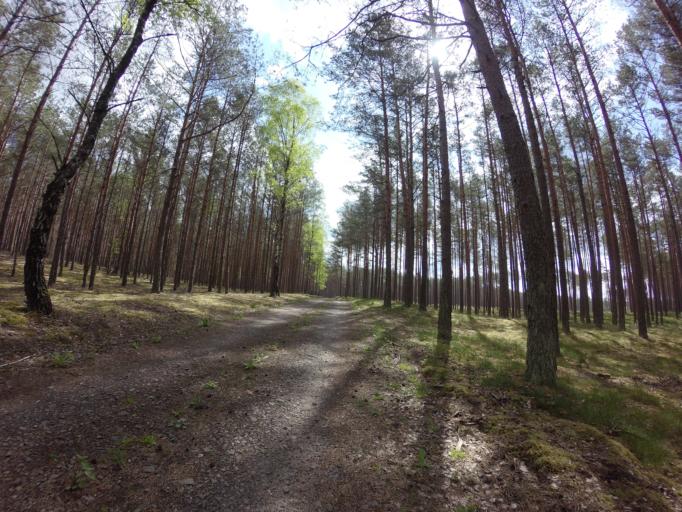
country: PL
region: West Pomeranian Voivodeship
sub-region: Powiat drawski
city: Kalisz Pomorski
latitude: 53.1993
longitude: 15.9985
